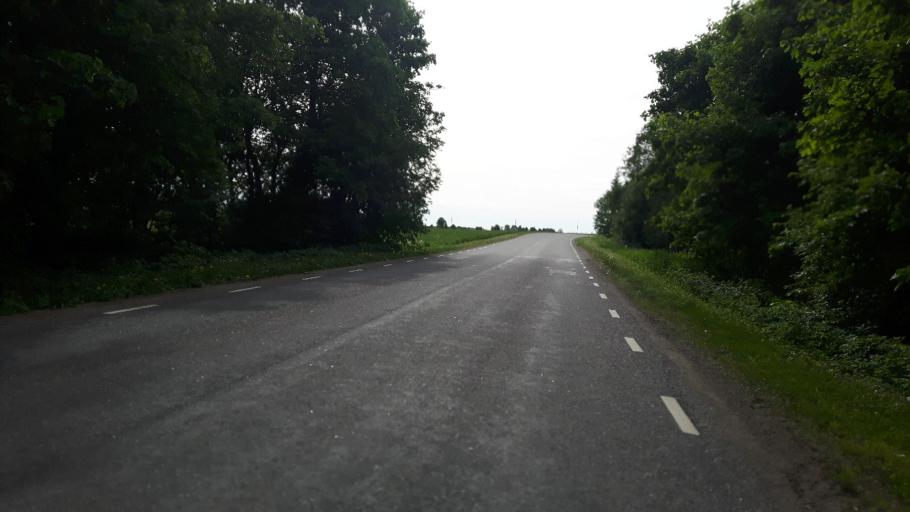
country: EE
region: Harju
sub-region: Maardu linn
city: Maardu
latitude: 59.4228
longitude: 25.0107
